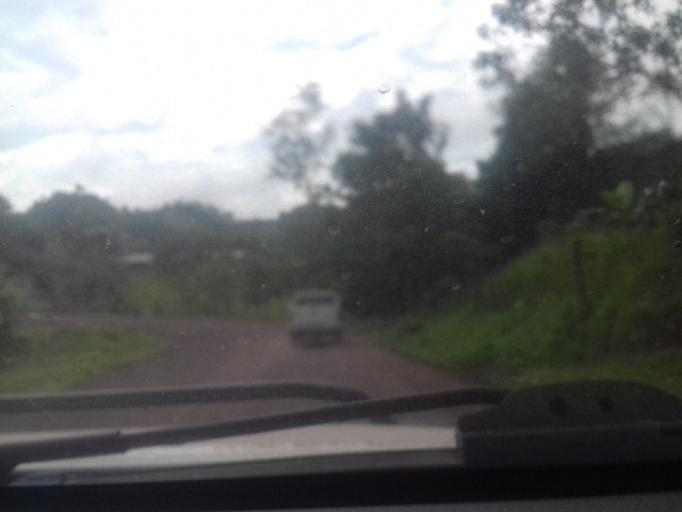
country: NI
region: Atlantico Norte (RAAN)
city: Waslala
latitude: 13.3898
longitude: -85.3286
